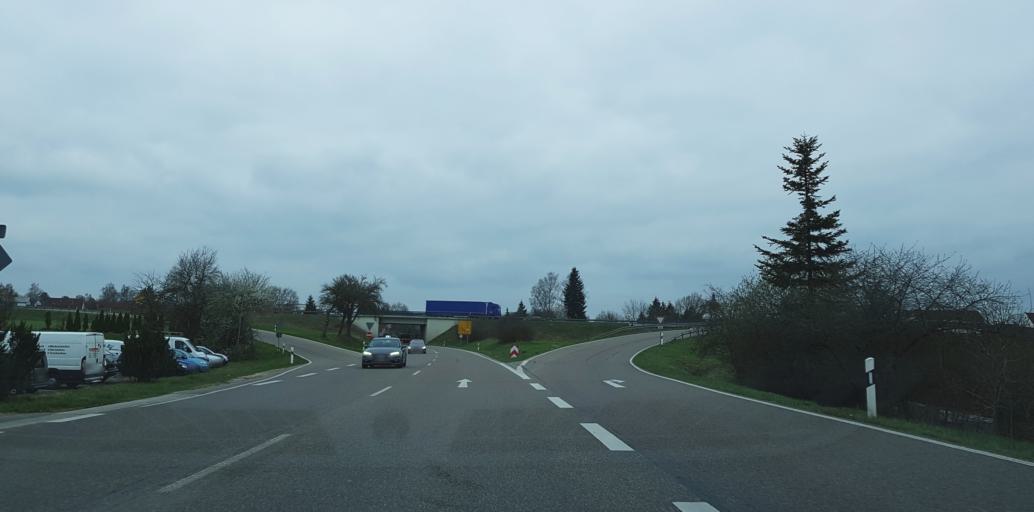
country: DE
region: Baden-Wuerttemberg
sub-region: Tuebingen Region
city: Ehingen
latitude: 48.2919
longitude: 9.7316
